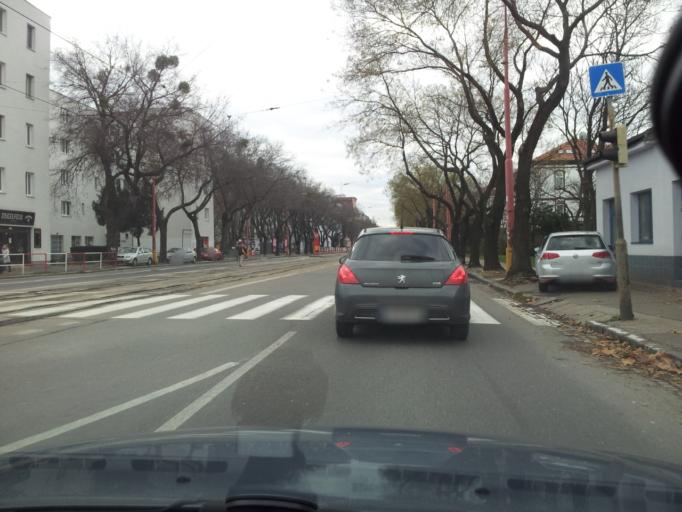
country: SK
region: Bratislavsky
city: Bratislava
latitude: 48.1657
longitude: 17.1353
